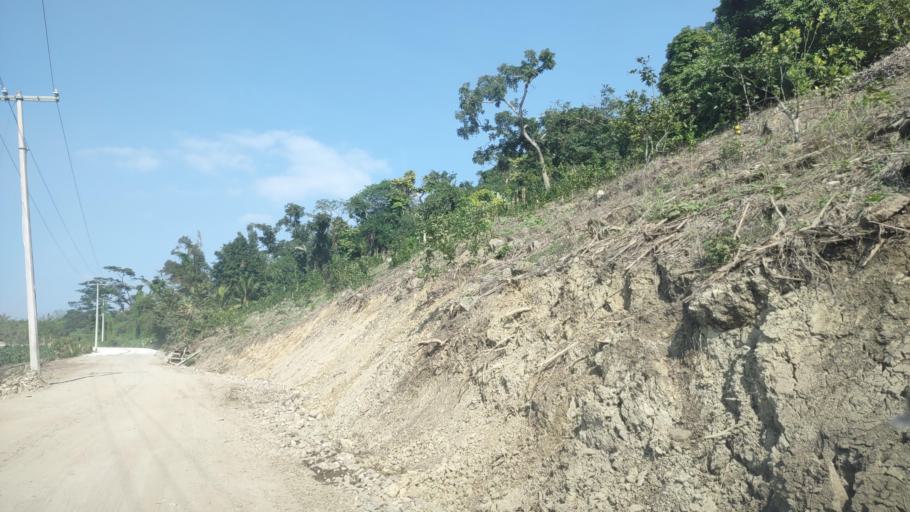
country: MX
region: Veracruz
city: Agua Dulce
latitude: 20.2985
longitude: -97.2825
